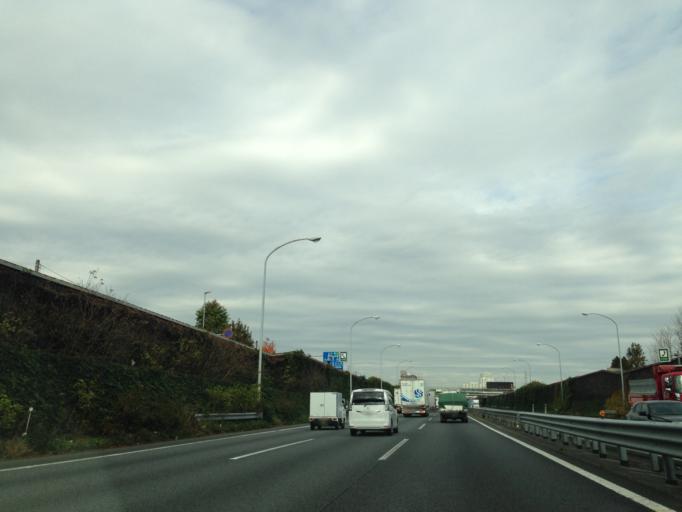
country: JP
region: Saitama
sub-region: Kawaguchi-shi
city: Hatogaya-honcho
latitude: 35.8621
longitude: 139.7347
